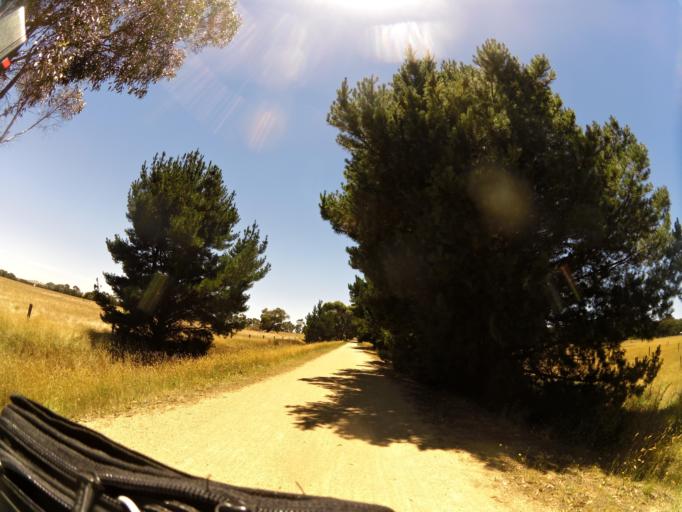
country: AU
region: Victoria
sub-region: Ballarat North
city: Delacombe
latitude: -37.5754
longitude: 143.7282
